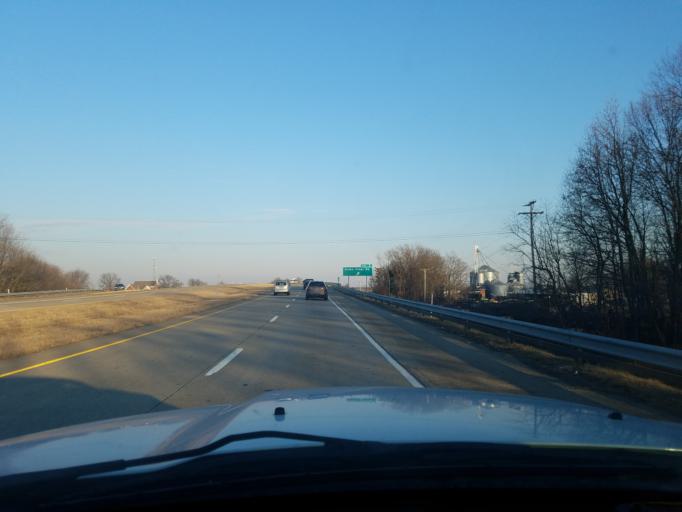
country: US
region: Indiana
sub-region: Vanderburgh County
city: Evansville
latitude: 37.9391
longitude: -87.4973
